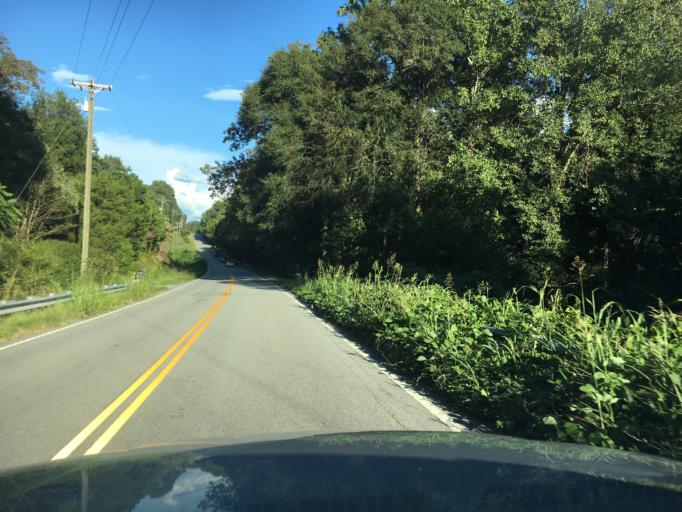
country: US
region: South Carolina
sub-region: Greenville County
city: Five Forks
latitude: 34.7929
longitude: -82.1359
